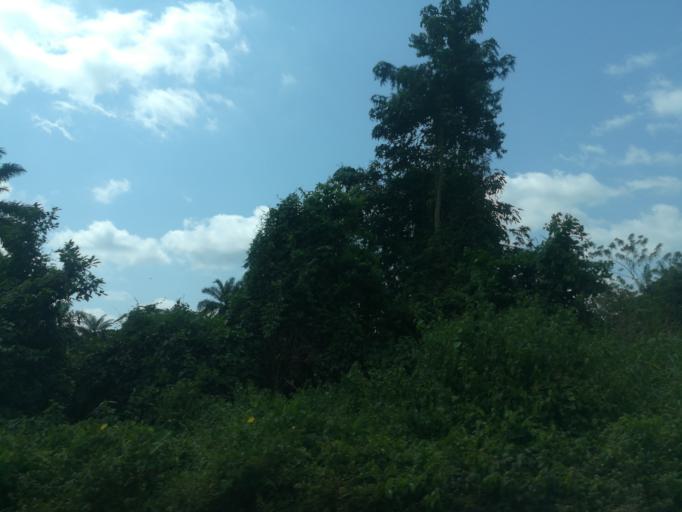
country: NG
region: Oyo
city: Moniya
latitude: 7.5836
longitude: 3.9112
